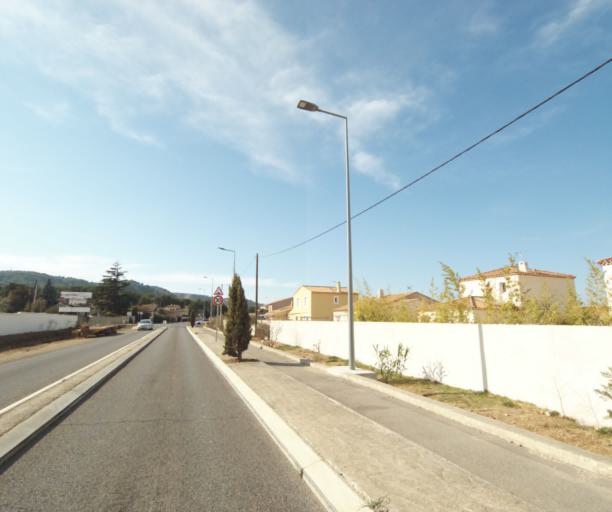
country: FR
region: Provence-Alpes-Cote d'Azur
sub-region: Departement des Bouches-du-Rhone
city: Chateauneuf-les-Martigues
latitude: 43.3805
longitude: 5.1788
